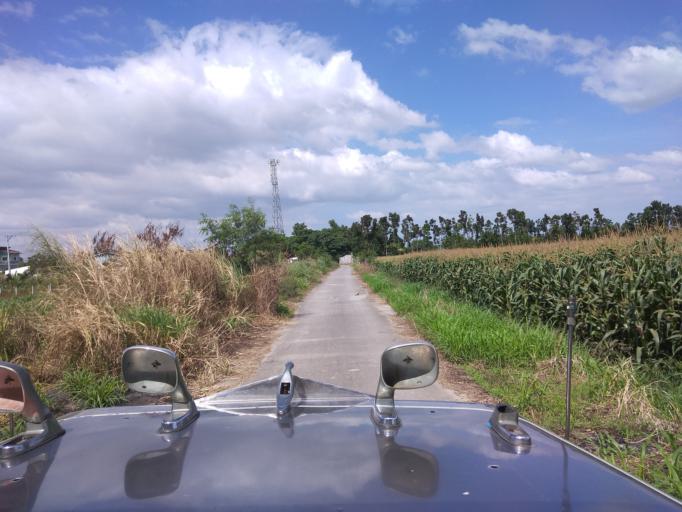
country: PH
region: Central Luzon
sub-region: Province of Pampanga
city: Anao
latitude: 15.1318
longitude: 120.6978
